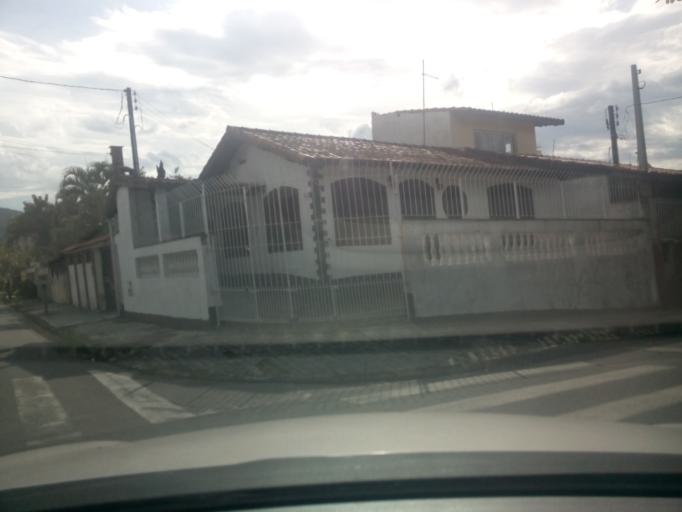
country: BR
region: Sao Paulo
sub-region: Peruibe
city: Peruibe
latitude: -24.3188
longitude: -46.9996
